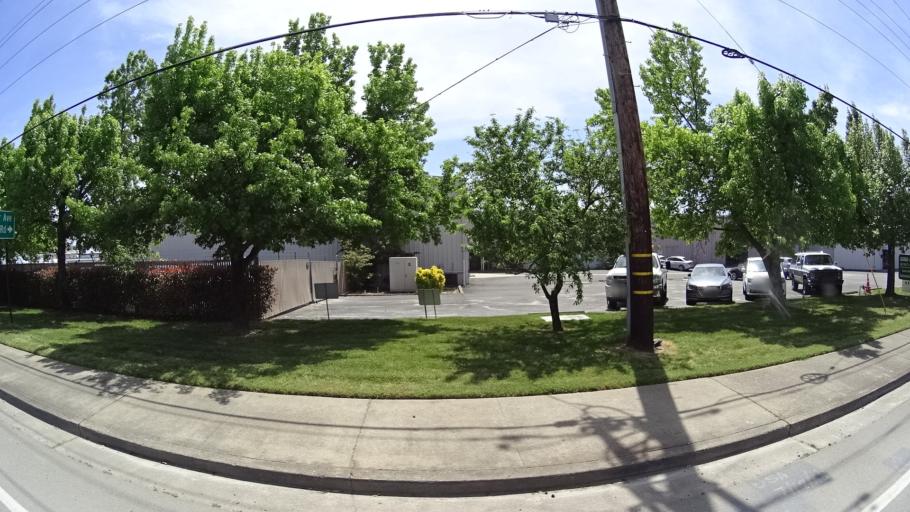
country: US
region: California
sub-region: Placer County
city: Rocklin
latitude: 38.8032
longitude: -121.2204
